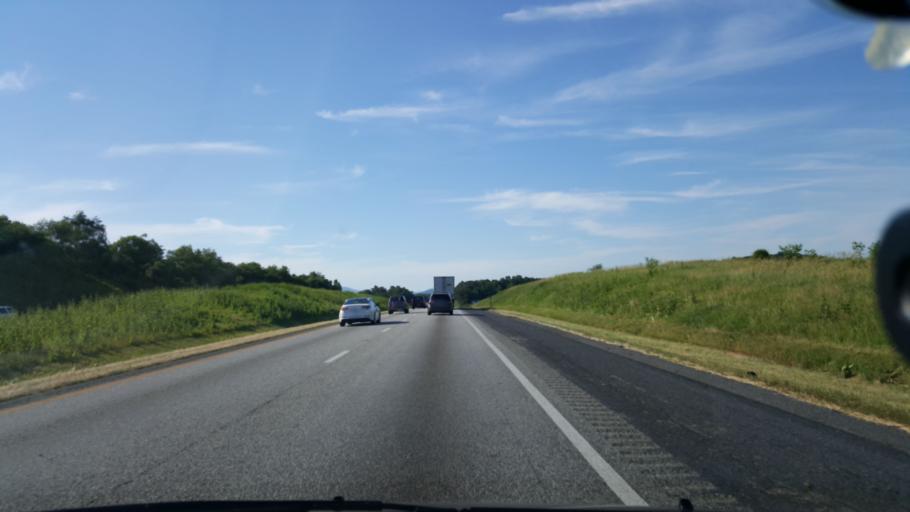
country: US
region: Virginia
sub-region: Augusta County
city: Weyers Cave
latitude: 38.3264
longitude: -78.9316
